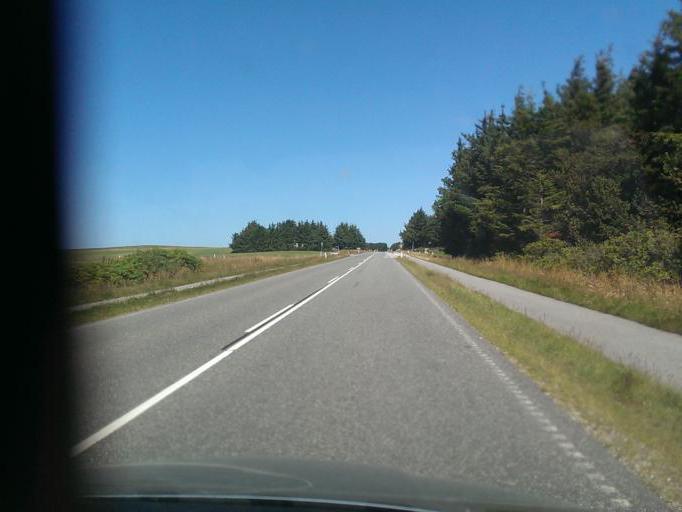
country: DK
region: North Denmark
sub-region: Jammerbugt Kommune
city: Pandrup
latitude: 57.3018
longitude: 9.6983
